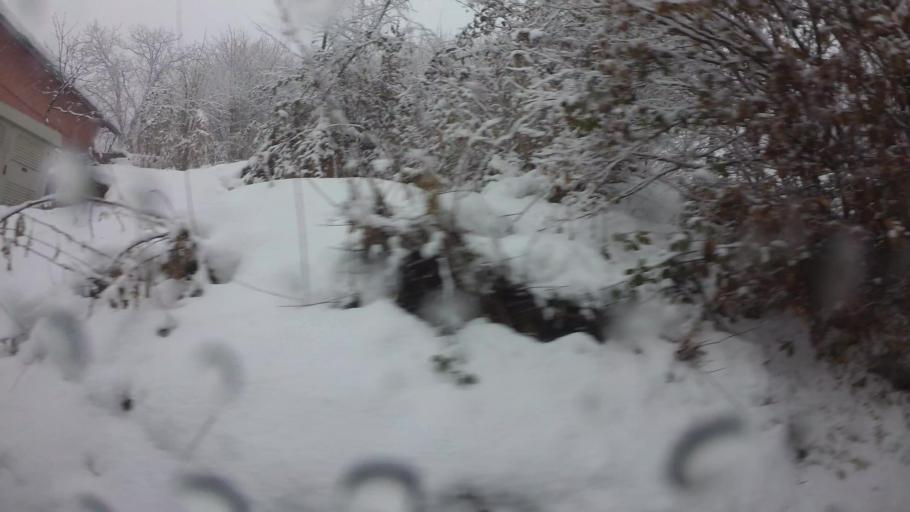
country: BA
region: Federation of Bosnia and Herzegovina
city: Kobilja Glava
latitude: 43.8507
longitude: 18.4495
